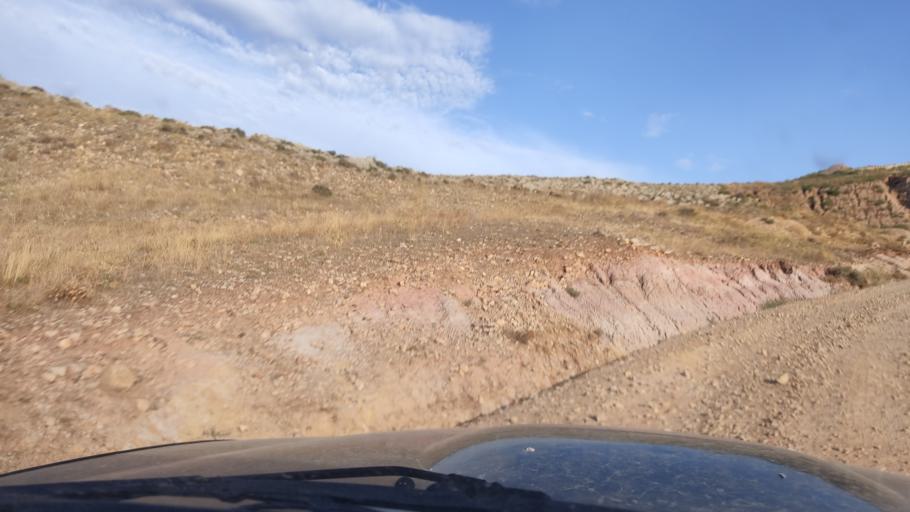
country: ES
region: Aragon
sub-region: Provincia de Teruel
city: Monforte de Moyuela
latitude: 41.0470
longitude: -0.9752
